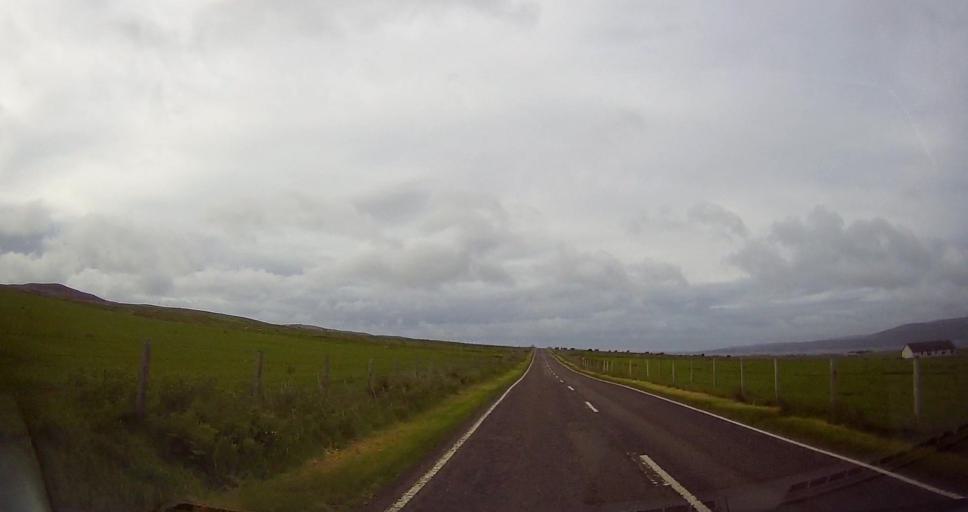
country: GB
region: Scotland
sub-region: Orkney Islands
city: Stromness
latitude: 58.9501
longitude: -3.2167
